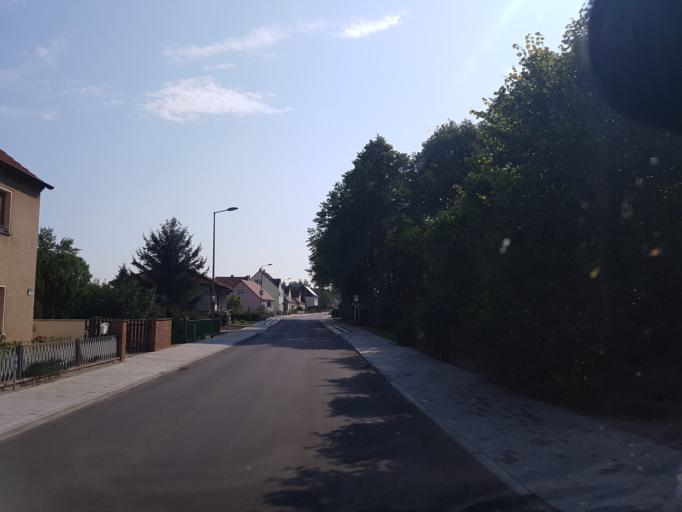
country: DE
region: Brandenburg
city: Lauchhammer
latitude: 51.5133
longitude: 13.7087
